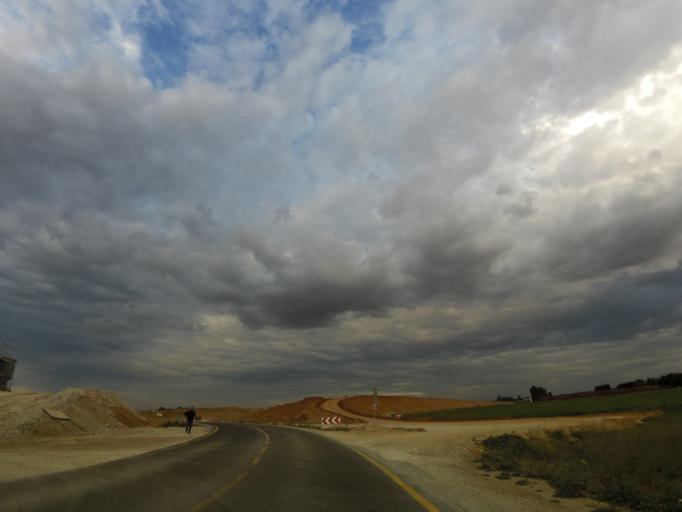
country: FR
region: Languedoc-Roussillon
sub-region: Departement du Gard
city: Vestric-et-Candiac
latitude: 43.7240
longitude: 4.2705
